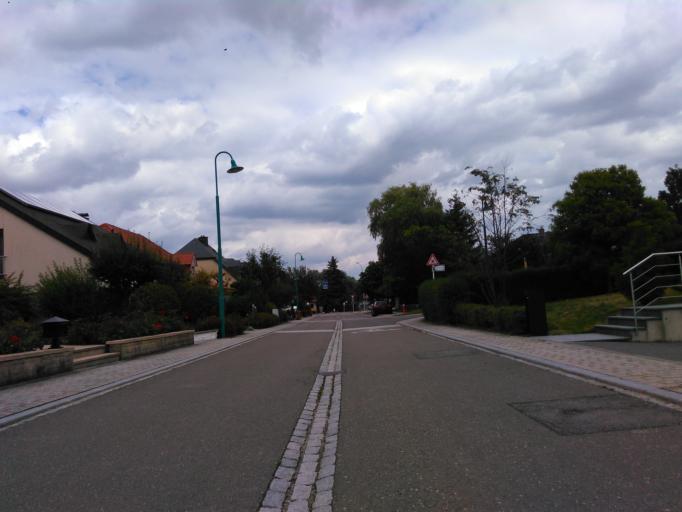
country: LU
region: Grevenmacher
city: Gonderange
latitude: 49.6917
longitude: 6.2522
